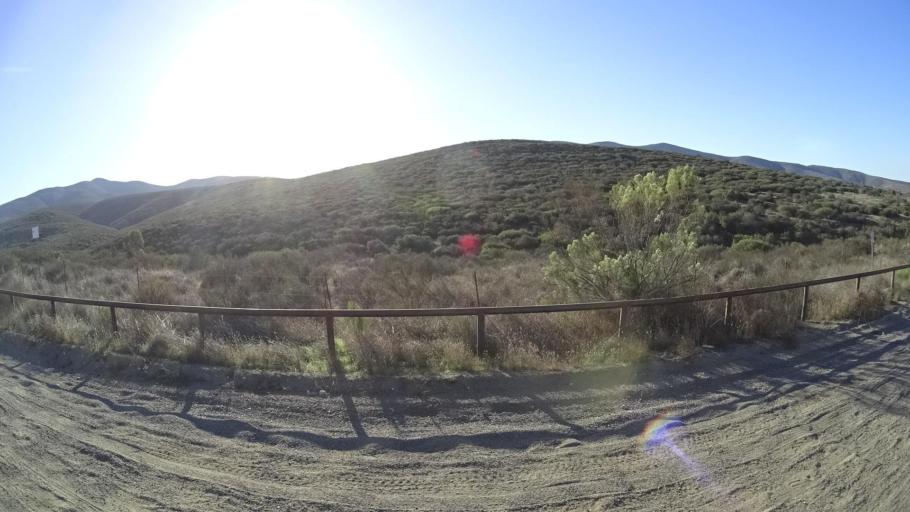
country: US
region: California
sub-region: San Diego County
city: Jamul
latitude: 32.6787
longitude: -116.9173
